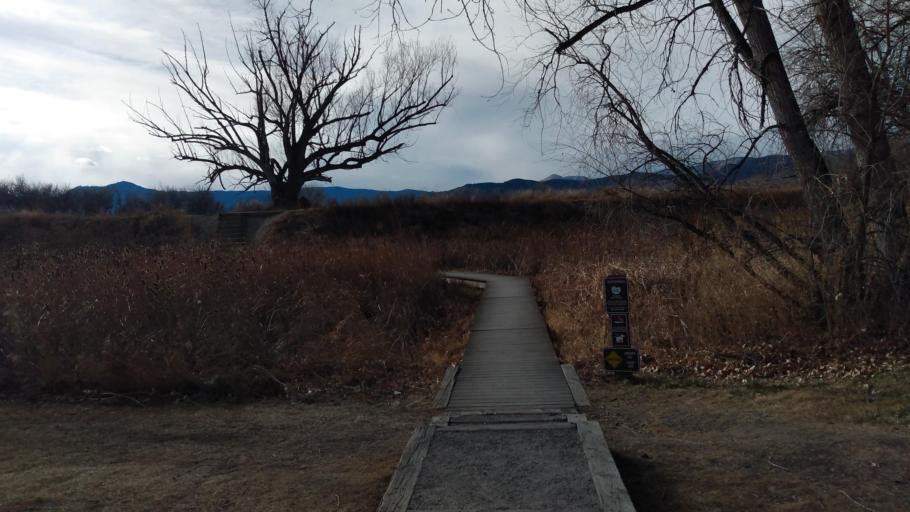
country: US
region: Colorado
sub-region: Boulder County
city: Gunbarrel
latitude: 40.0632
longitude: -105.1959
